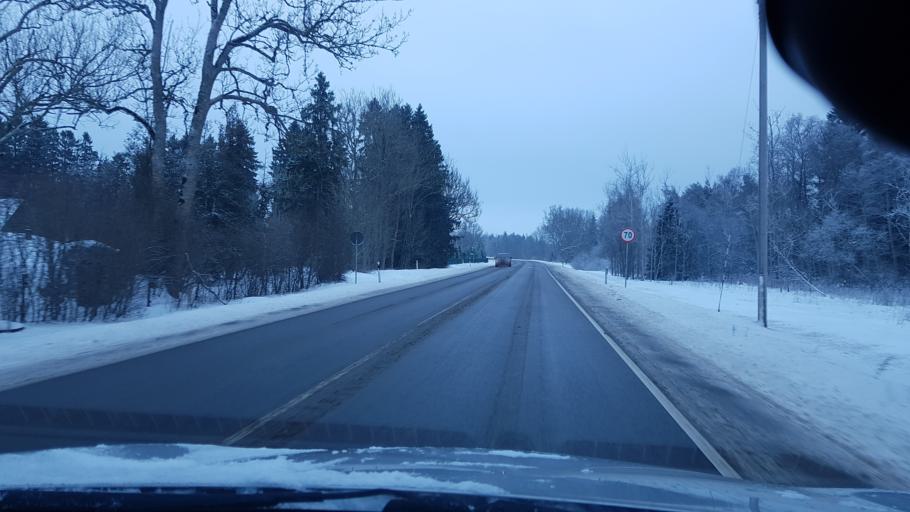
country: EE
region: Harju
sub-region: Keila linn
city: Keila
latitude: 59.3399
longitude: 24.2704
